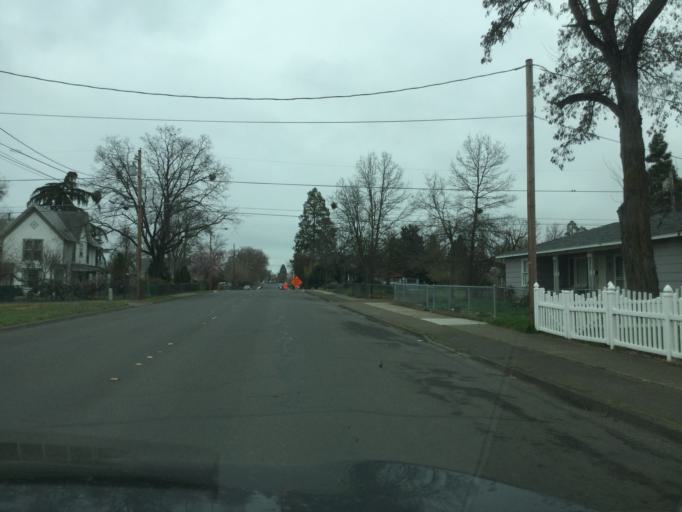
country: US
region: Oregon
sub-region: Jackson County
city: Central Point
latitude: 42.3786
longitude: -122.9186
